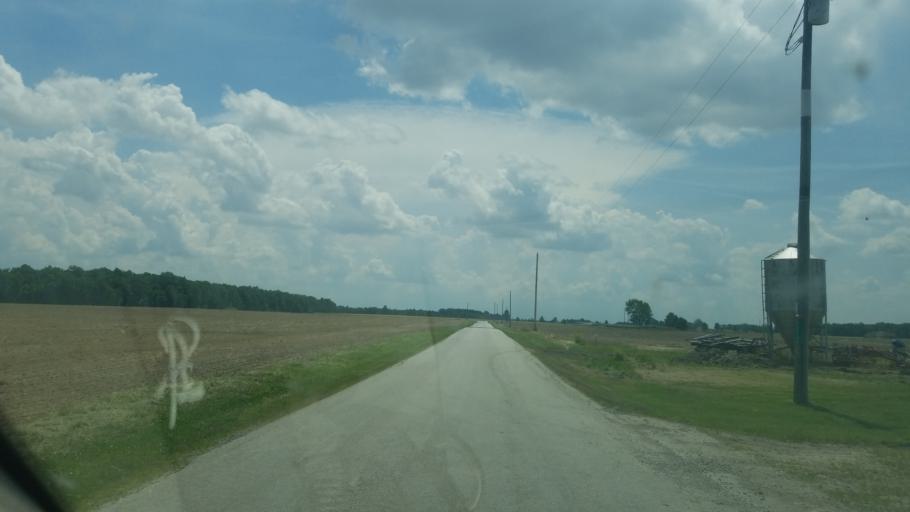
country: US
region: Ohio
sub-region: Hancock County
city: Arlington
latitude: 40.8229
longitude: -83.6001
